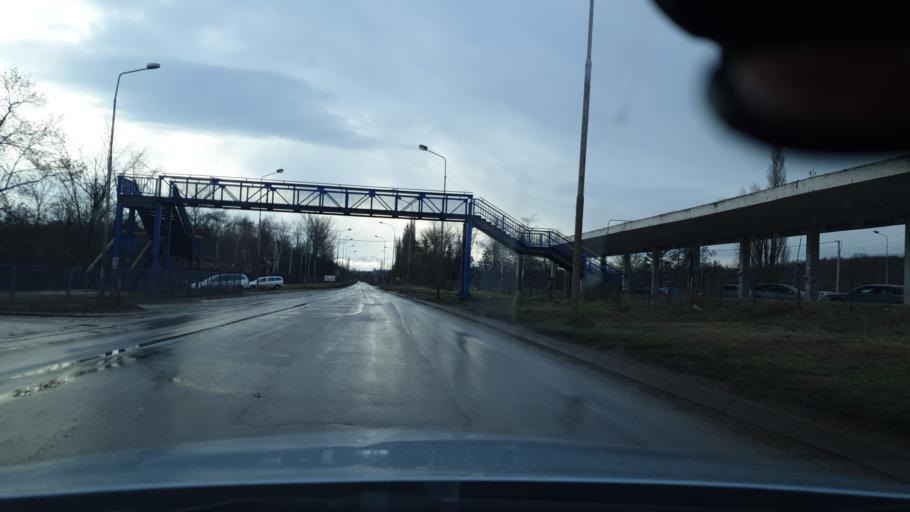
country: RS
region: Central Serbia
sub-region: Podunavski Okrug
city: Smederevo
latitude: 44.6052
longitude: 20.9616
